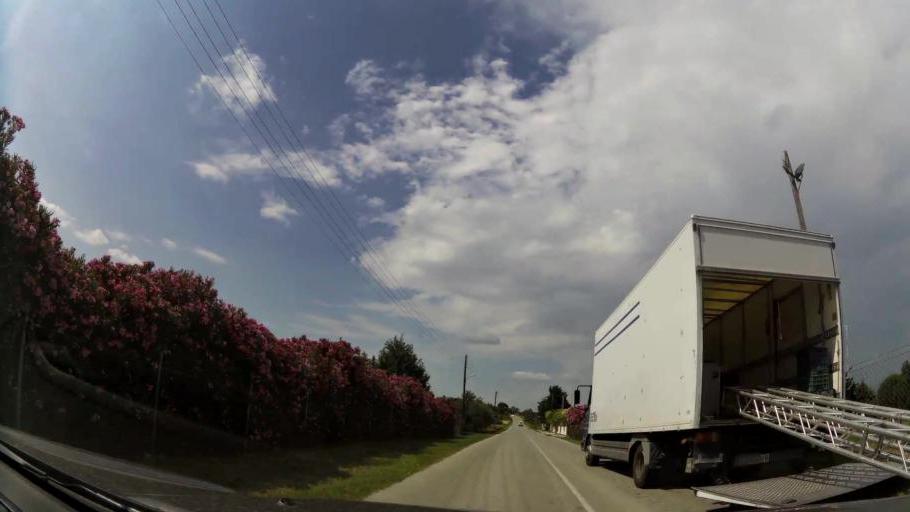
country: GR
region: Central Macedonia
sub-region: Nomos Pierias
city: Makrygialos
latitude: 40.3978
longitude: 22.6169
